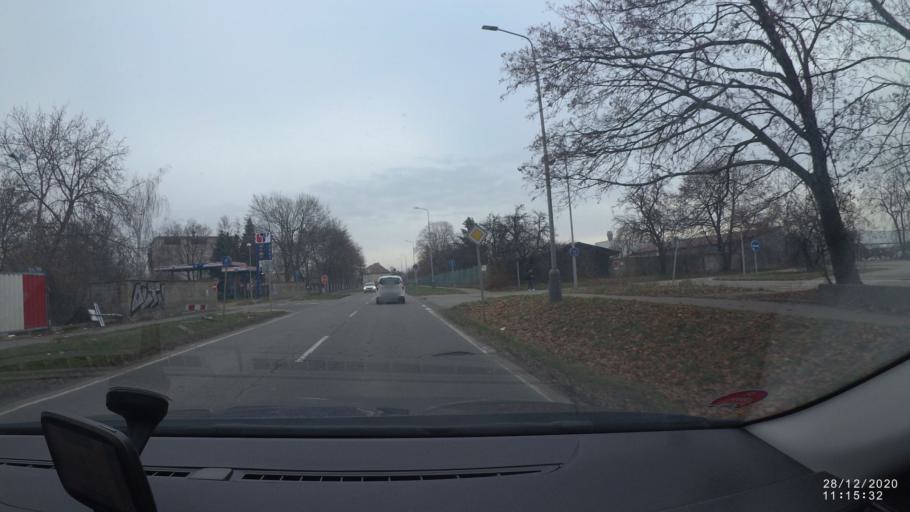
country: CZ
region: Praha
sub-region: Praha 18
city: Letnany
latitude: 50.1298
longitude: 14.5118
